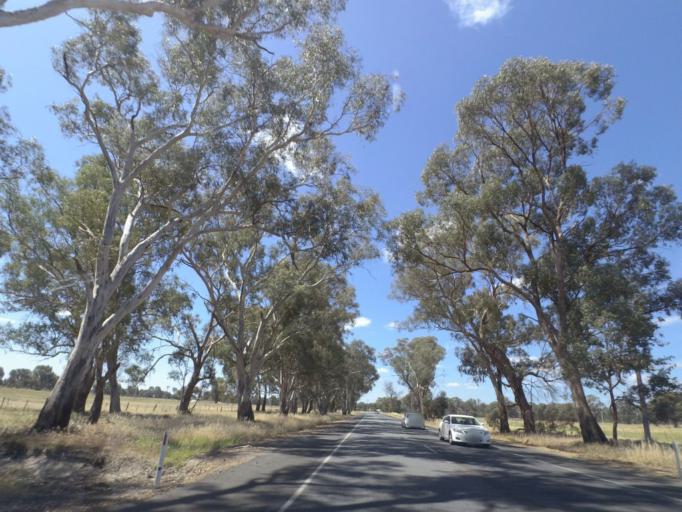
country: AU
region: Victoria
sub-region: Wangaratta
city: Wangaratta
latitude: -36.4012
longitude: 146.2766
